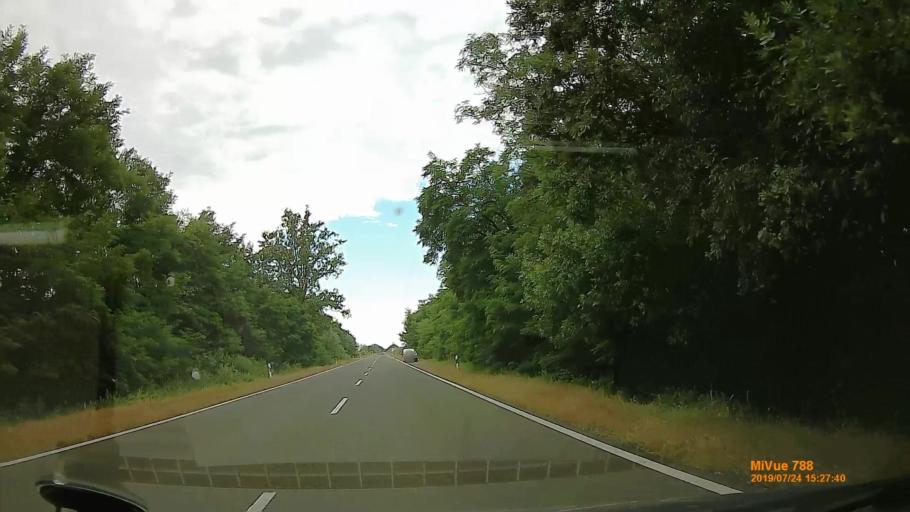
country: HU
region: Szabolcs-Szatmar-Bereg
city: Tarpa
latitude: 48.1607
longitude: 22.4953
